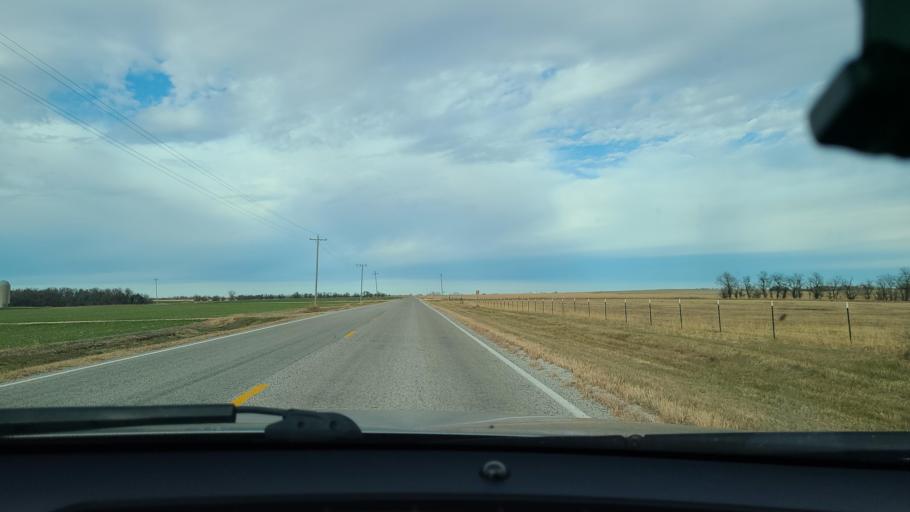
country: US
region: Kansas
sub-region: McPherson County
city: Inman
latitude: 38.3164
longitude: -97.9247
